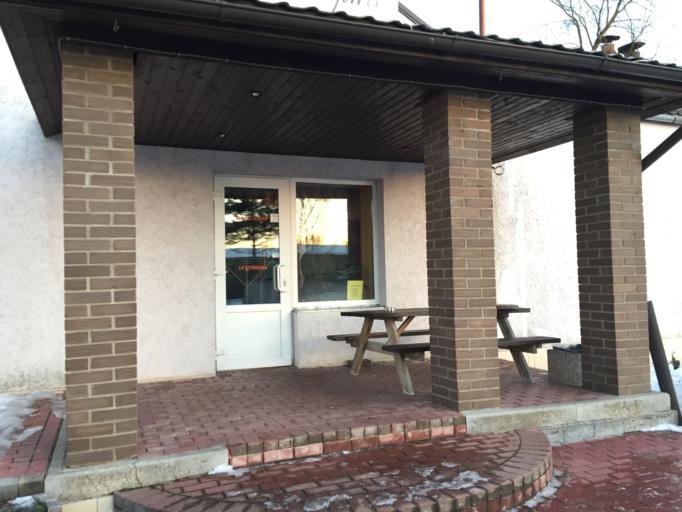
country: LV
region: Jaunjelgava
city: Jaunjelgava
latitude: 56.6174
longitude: 25.0904
